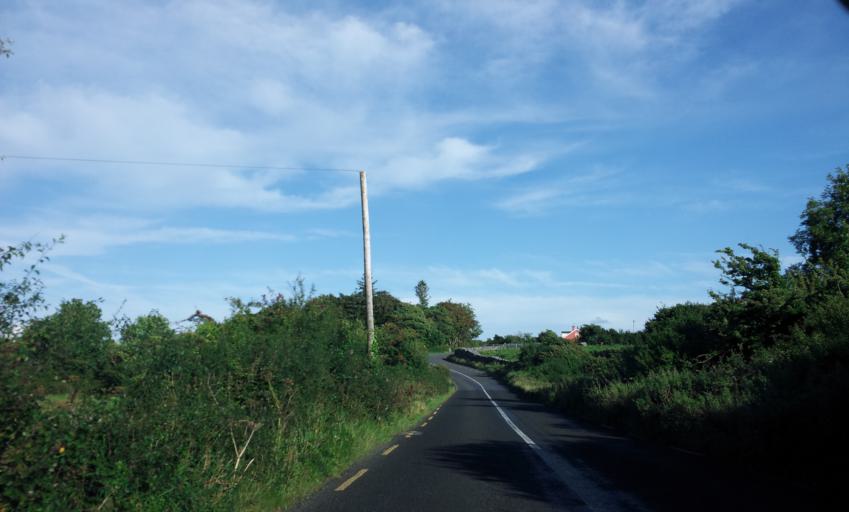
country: IE
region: Munster
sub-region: An Clar
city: Ennis
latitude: 52.9771
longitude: -9.1042
